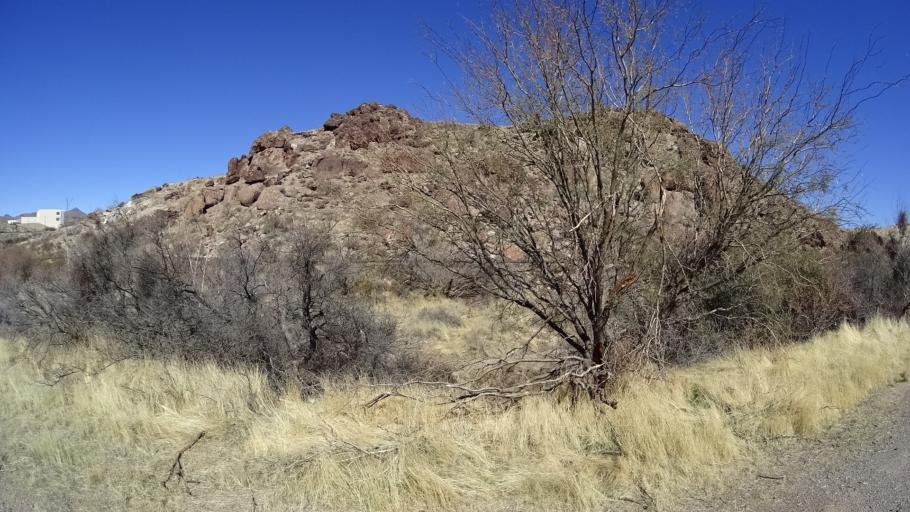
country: US
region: Arizona
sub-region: Mohave County
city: Kingman
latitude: 35.1816
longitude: -114.0602
